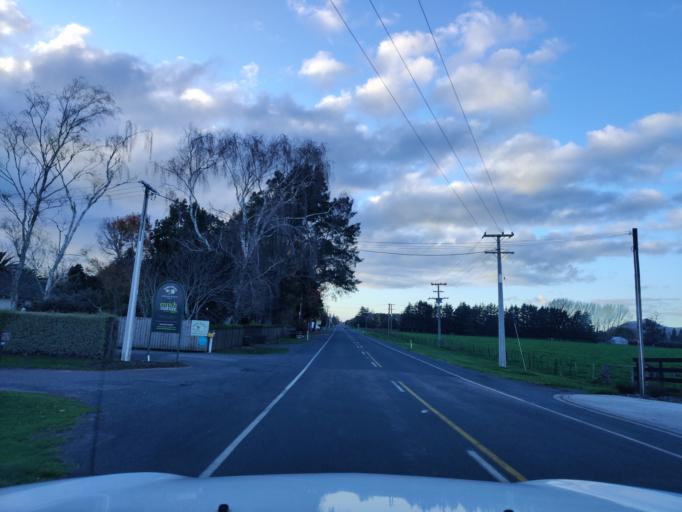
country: NZ
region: Waikato
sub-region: Waipa District
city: Cambridge
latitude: -37.8663
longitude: 175.4390
